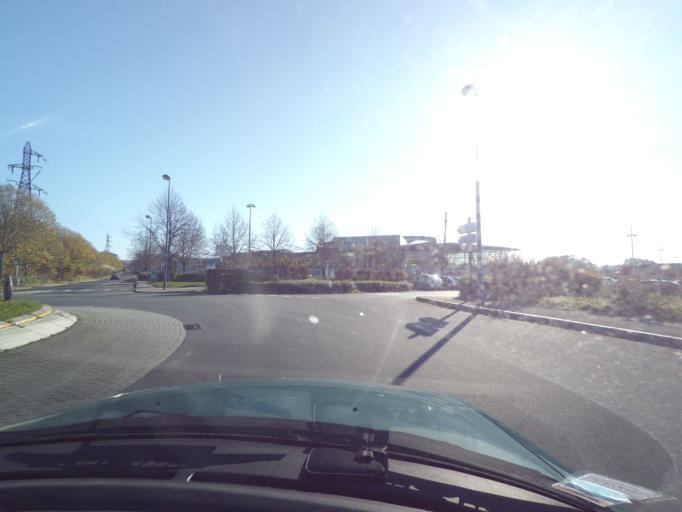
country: FR
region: Pays de la Loire
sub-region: Departement de la Loire-Atlantique
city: Sainte-Luce-sur-Loire
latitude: 47.2489
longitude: -1.5179
